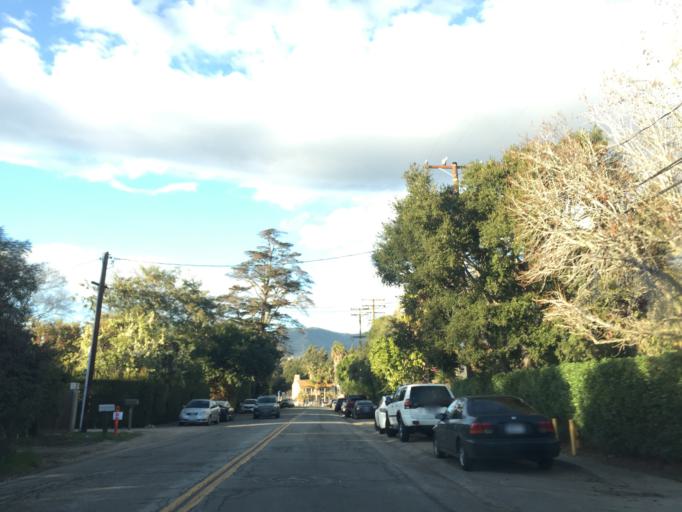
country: US
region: California
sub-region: Santa Barbara County
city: Goleta
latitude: 34.4383
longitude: -119.7711
